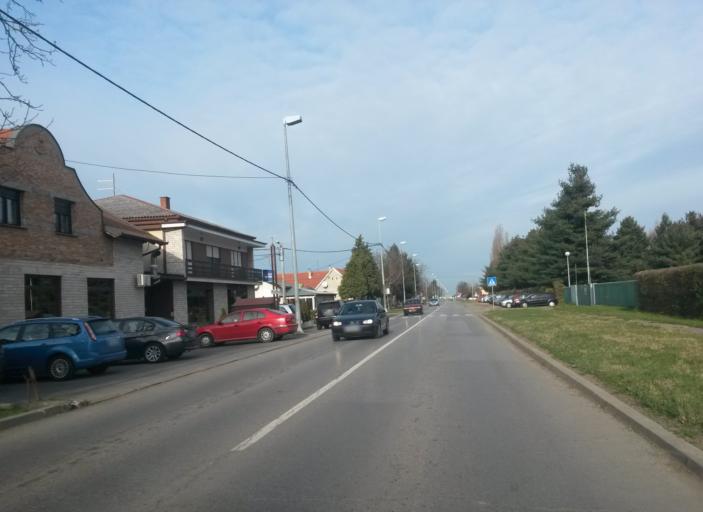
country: HR
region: Osjecko-Baranjska
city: Viskovci
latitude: 45.3266
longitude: 18.4182
